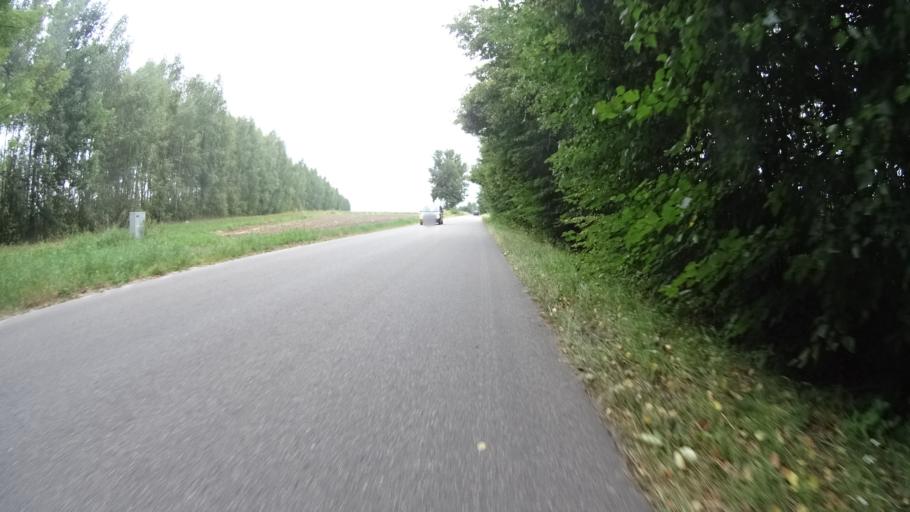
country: PL
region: Masovian Voivodeship
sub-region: Powiat grojecki
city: Goszczyn
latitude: 51.6842
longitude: 20.8613
